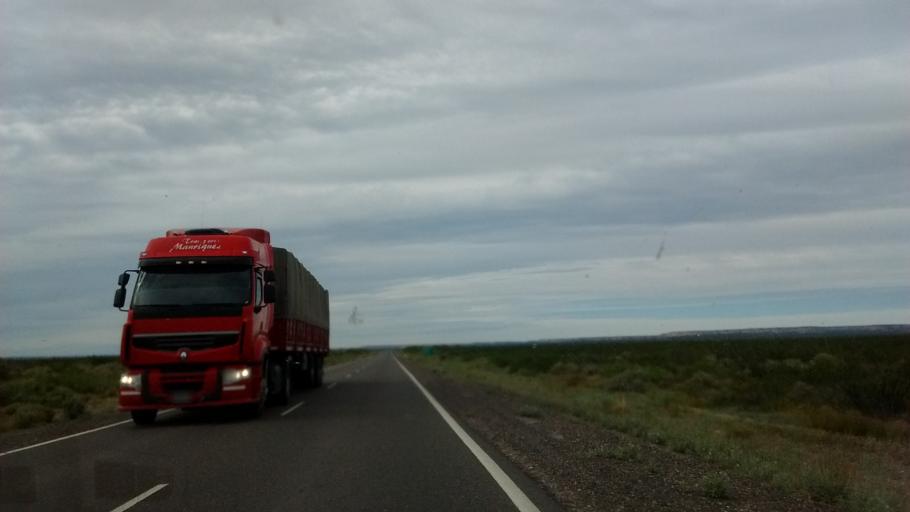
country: AR
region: Rio Negro
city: Catriel
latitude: -38.0796
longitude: -67.9245
